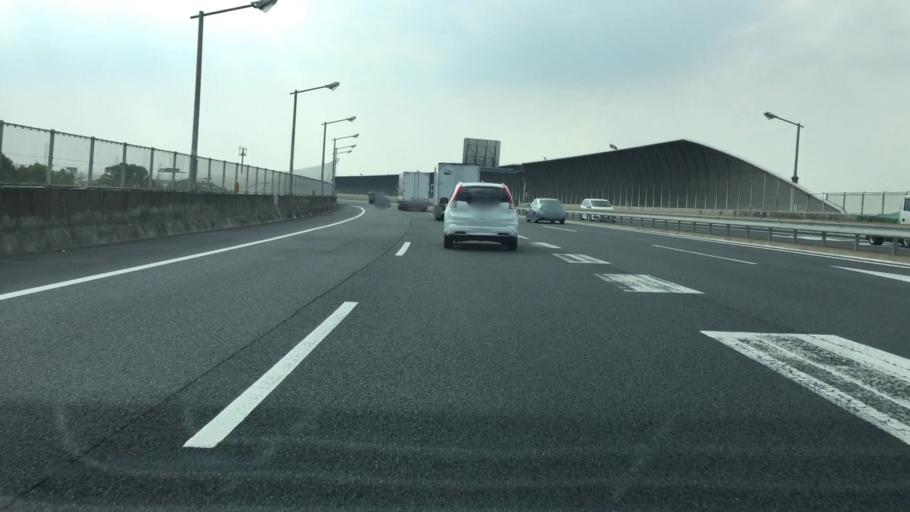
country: JP
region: Saitama
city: Yashio-shi
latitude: 35.8425
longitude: 139.8524
